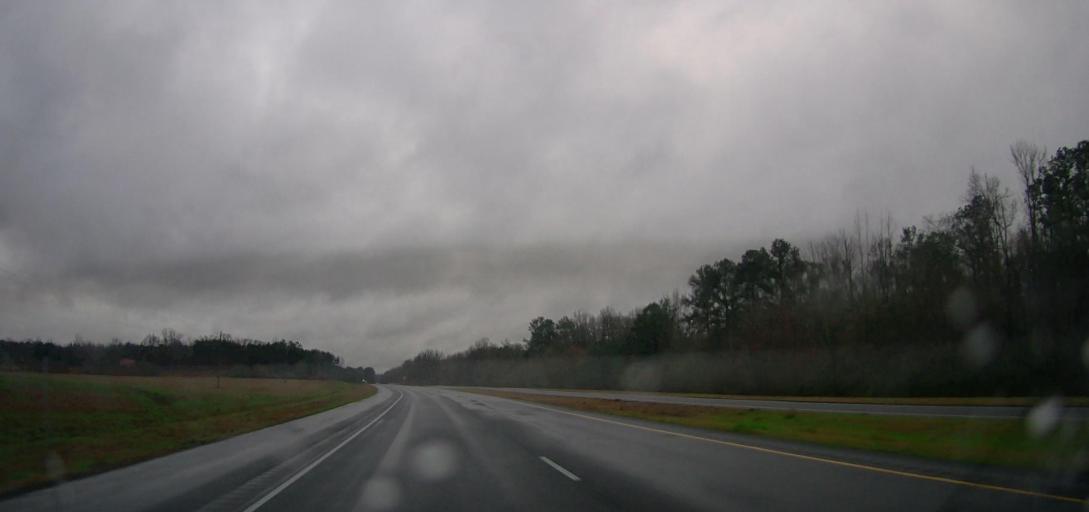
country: US
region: Alabama
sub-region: Bibb County
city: Centreville
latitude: 32.9336
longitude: -87.0601
